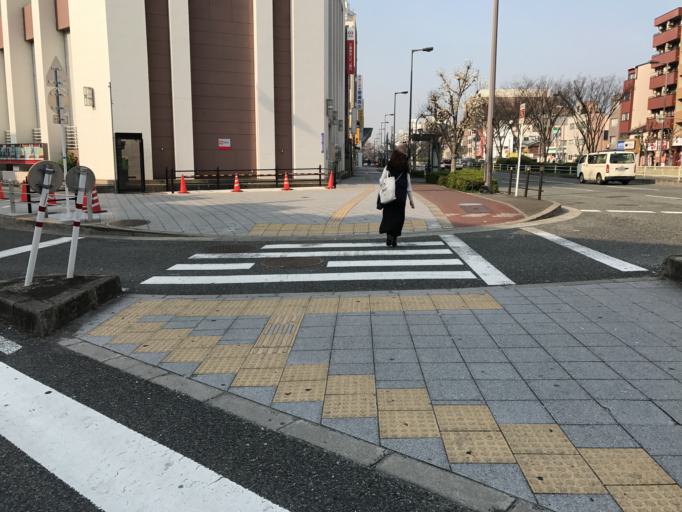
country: JP
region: Osaka
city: Osaka-shi
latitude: 34.6932
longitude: 135.4748
